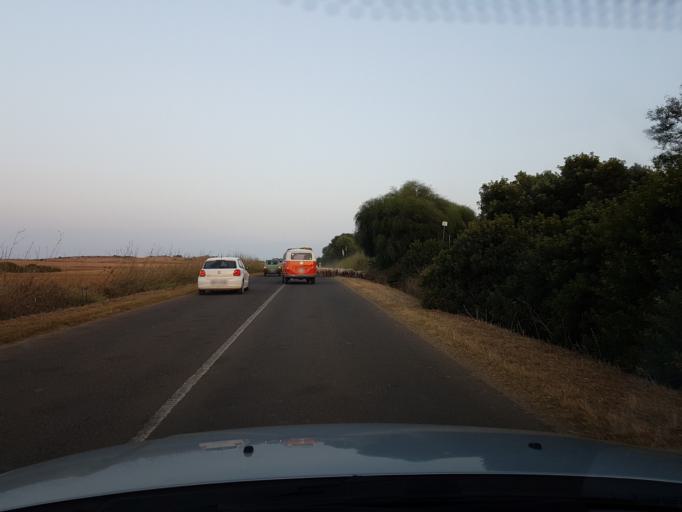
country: IT
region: Sardinia
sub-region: Provincia di Oristano
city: Cabras
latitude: 39.9358
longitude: 8.4449
